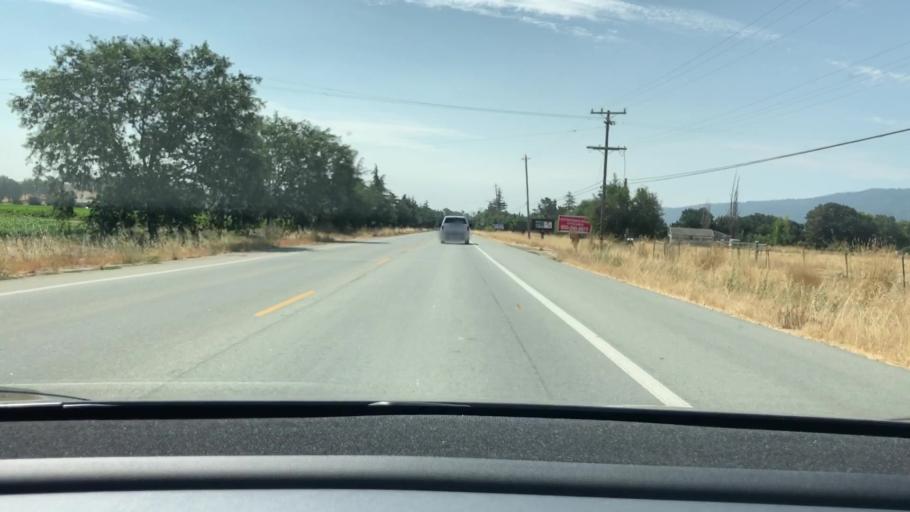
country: US
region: California
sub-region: Santa Clara County
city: San Martin
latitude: 37.0477
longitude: -121.6023
